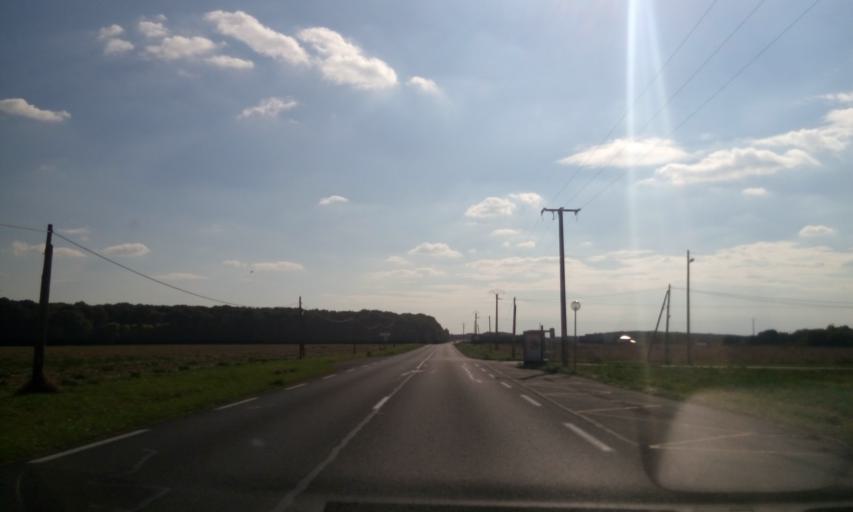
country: FR
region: Centre
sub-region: Departement d'Indre-et-Loire
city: Poce-sur-Cisse
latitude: 47.4835
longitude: 1.0085
